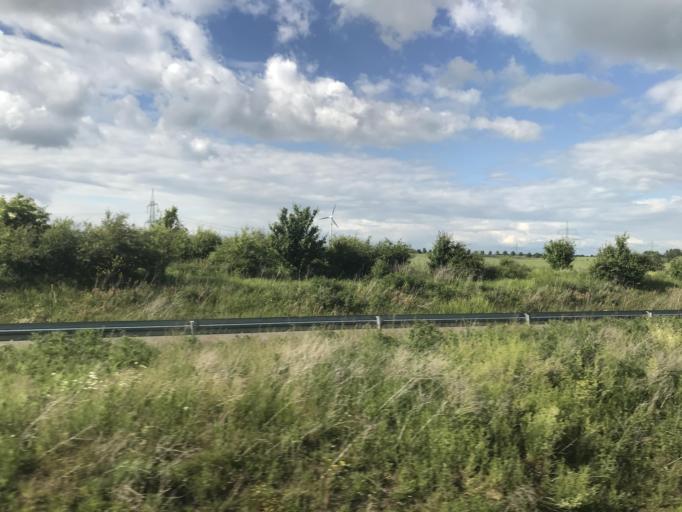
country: DE
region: Saxony-Anhalt
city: Langeneichstadt
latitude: 51.3265
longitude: 11.7478
